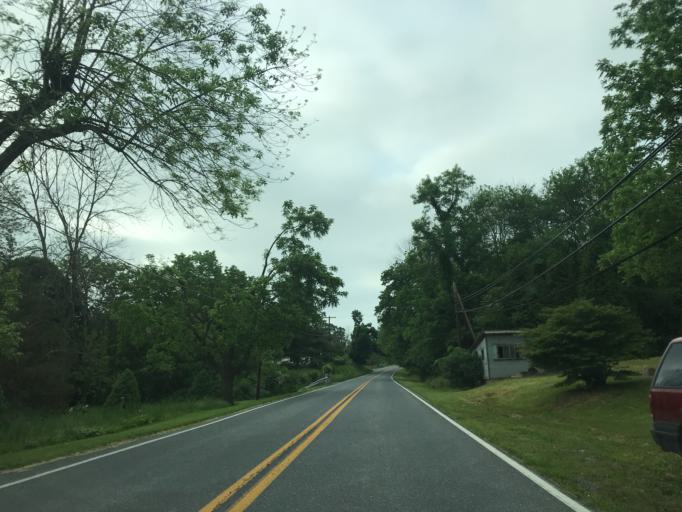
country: US
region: Maryland
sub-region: Frederick County
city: Clover Hill
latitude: 39.4978
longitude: -77.4020
